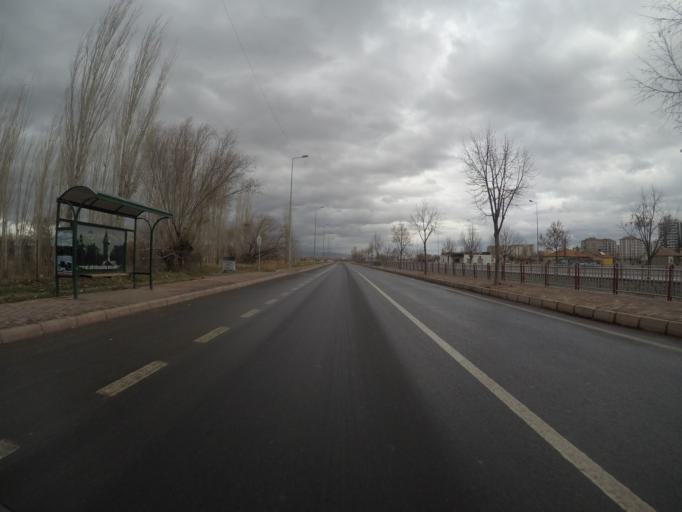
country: TR
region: Kayseri
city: Kayseri
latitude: 38.7528
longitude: 35.4764
